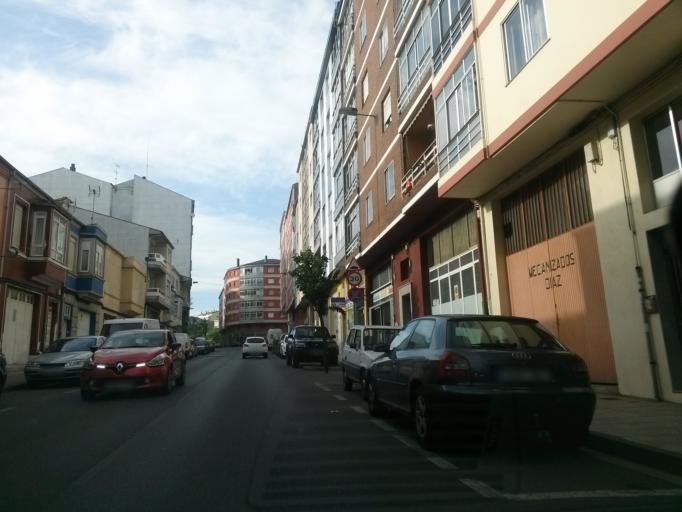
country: ES
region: Galicia
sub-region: Provincia de Lugo
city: Lugo
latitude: 43.0172
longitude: -7.5671
